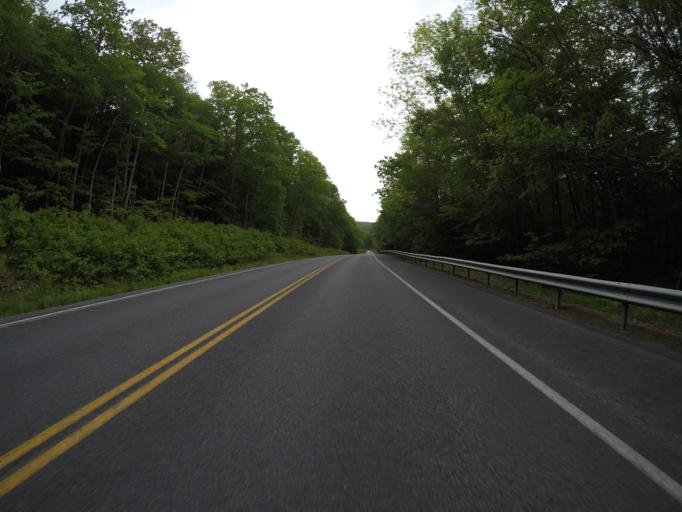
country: US
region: New York
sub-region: Sullivan County
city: Livingston Manor
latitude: 42.0597
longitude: -74.9222
